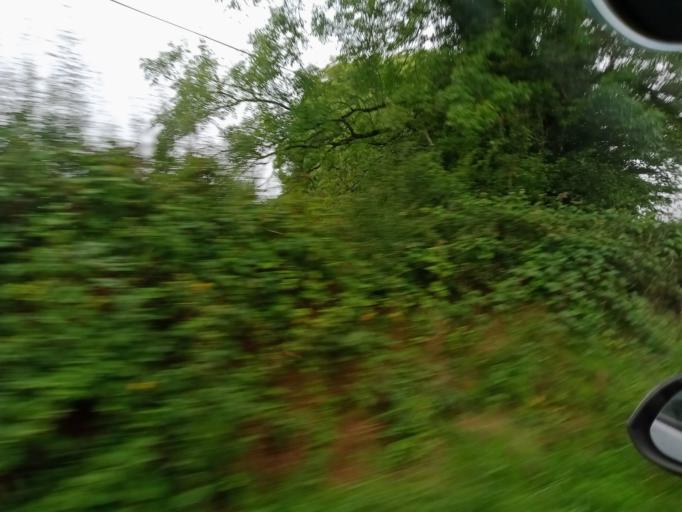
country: IE
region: Leinster
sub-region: Kilkenny
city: Castlecomer
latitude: 52.8526
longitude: -7.1736
